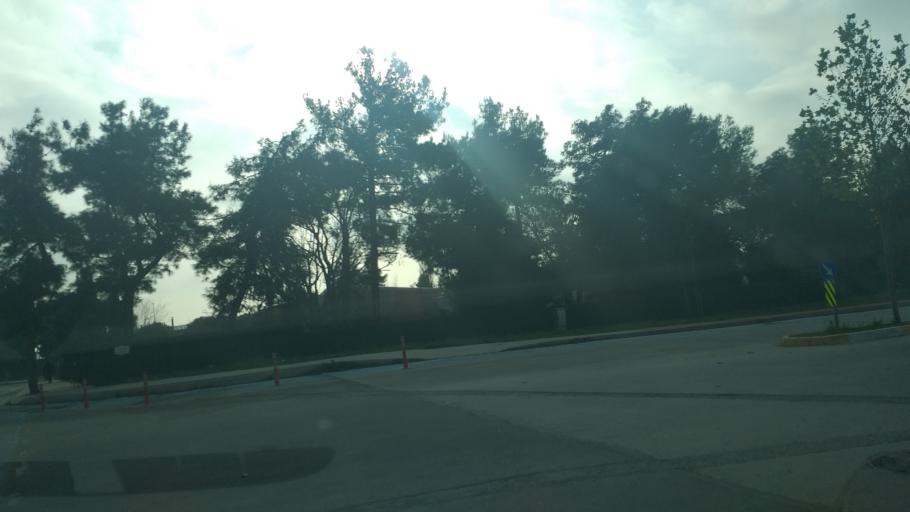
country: TR
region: Istanbul
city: merter keresteciler
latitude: 41.0290
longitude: 28.8873
